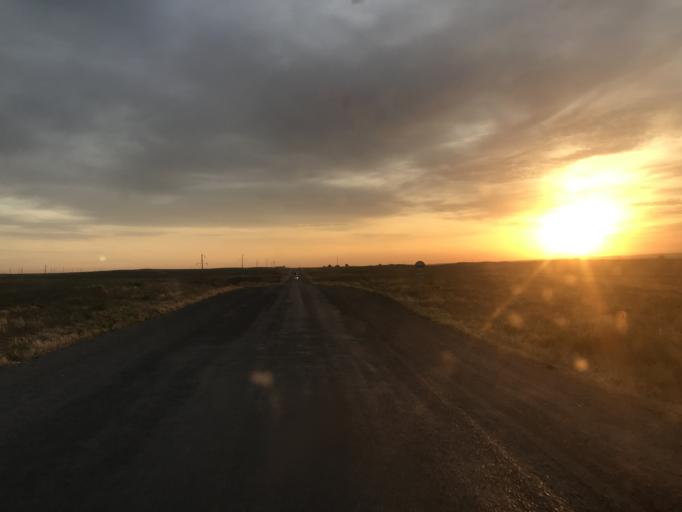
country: UZ
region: Toshkent
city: Zafar
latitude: 41.1775
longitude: 68.7633
